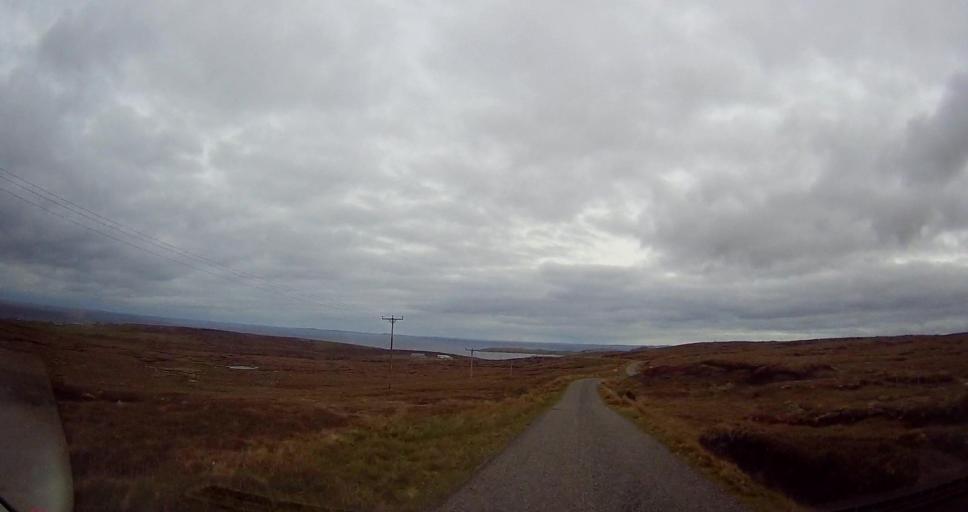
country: GB
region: Scotland
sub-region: Shetland Islands
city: Shetland
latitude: 60.5651
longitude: -1.0654
